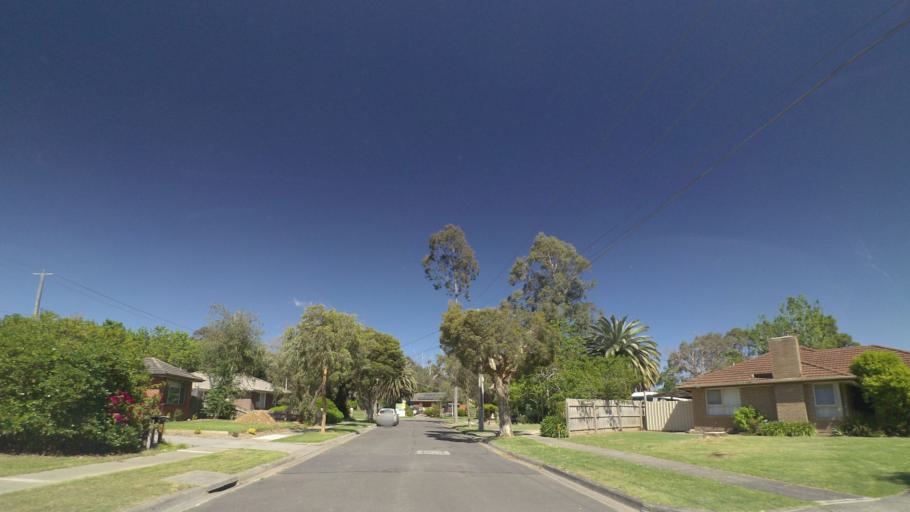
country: AU
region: Victoria
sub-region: Yarra Ranges
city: Kilsyth
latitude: -37.7964
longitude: 145.3167
